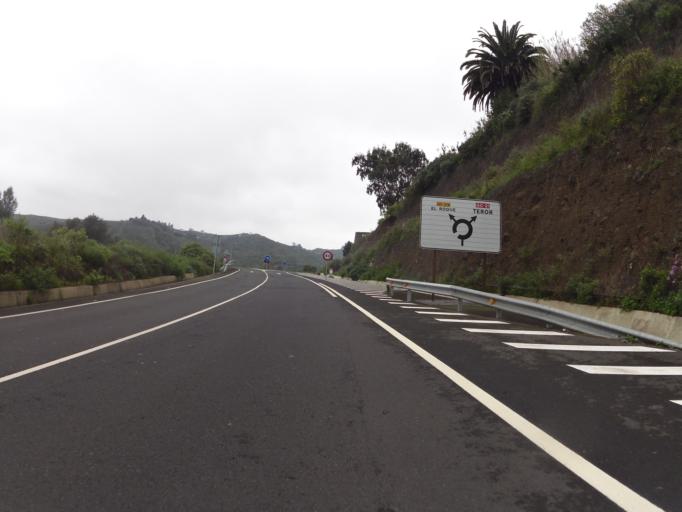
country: ES
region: Canary Islands
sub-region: Provincia de Las Palmas
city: Teror
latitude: 28.0687
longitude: -15.5374
